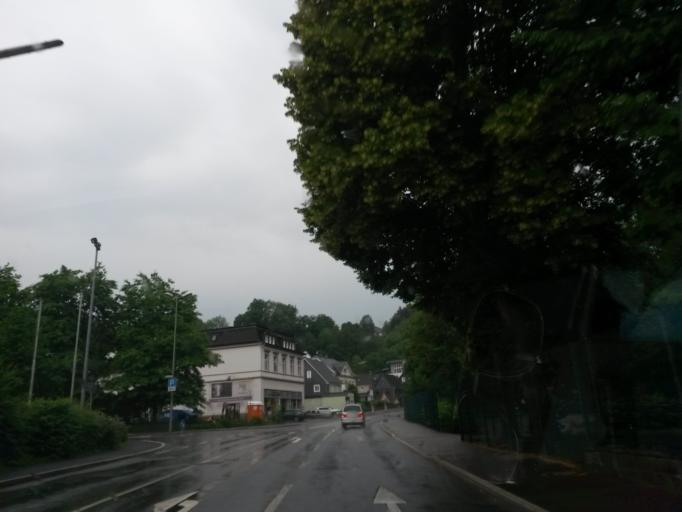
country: DE
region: North Rhine-Westphalia
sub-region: Regierungsbezirk Koln
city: Gummersbach
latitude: 51.0282
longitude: 7.5617
